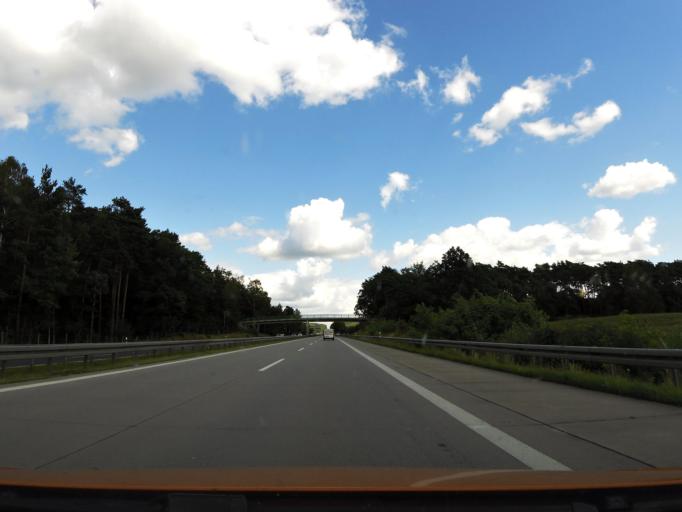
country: DE
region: Brandenburg
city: Joachimsthal
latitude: 52.8959
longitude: 13.7253
